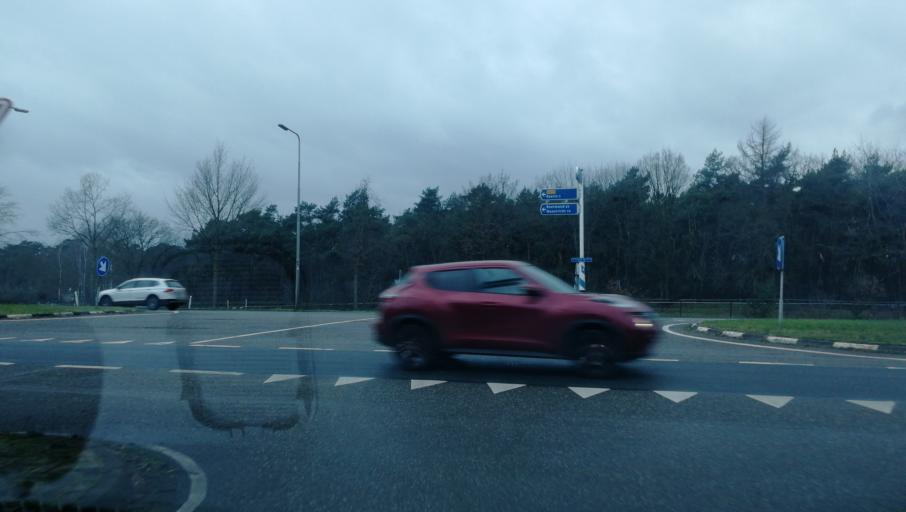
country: NL
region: Limburg
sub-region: Gemeente Venlo
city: Tegelen
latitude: 51.3501
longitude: 6.1125
